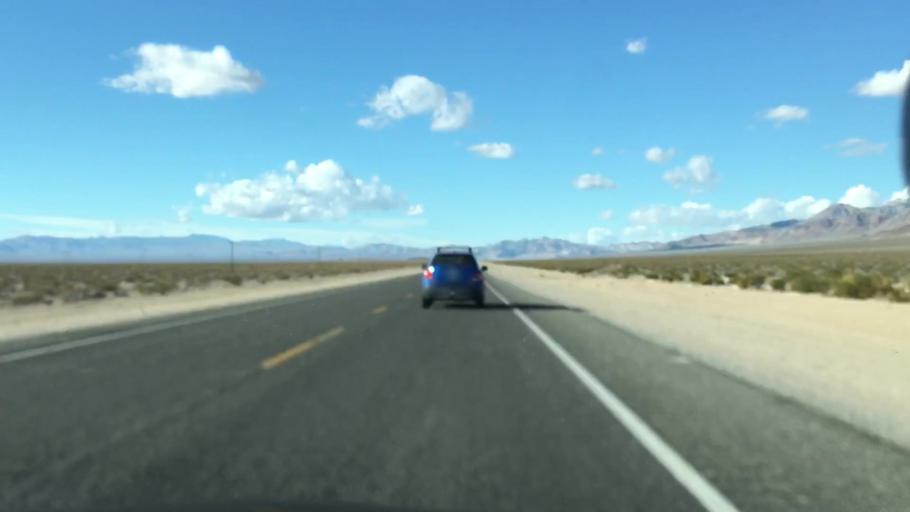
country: US
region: Nevada
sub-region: Nye County
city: Beatty
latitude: 36.7346
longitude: -116.6367
